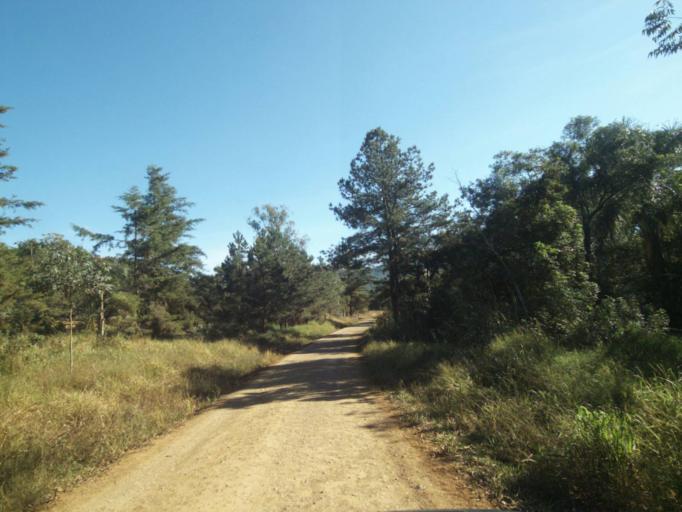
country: BR
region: Parana
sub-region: Tibagi
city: Tibagi
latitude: -24.5446
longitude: -50.5086
